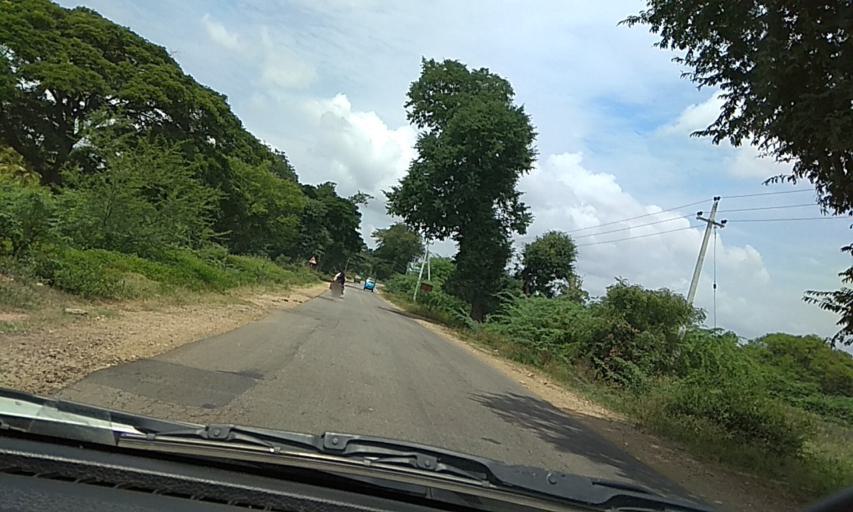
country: IN
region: Karnataka
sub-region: Chamrajnagar
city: Gundlupet
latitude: 11.8105
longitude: 76.7231
